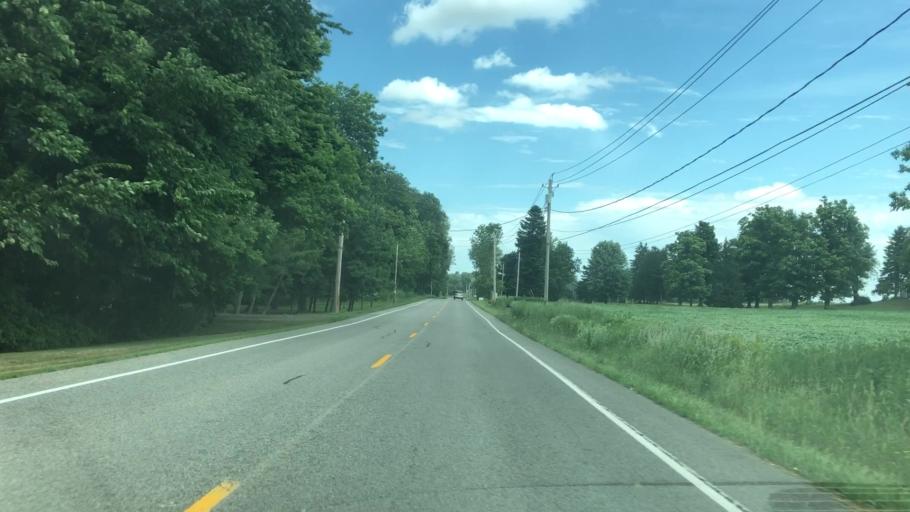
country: US
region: New York
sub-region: Wayne County
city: Macedon
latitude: 43.1143
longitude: -77.3524
